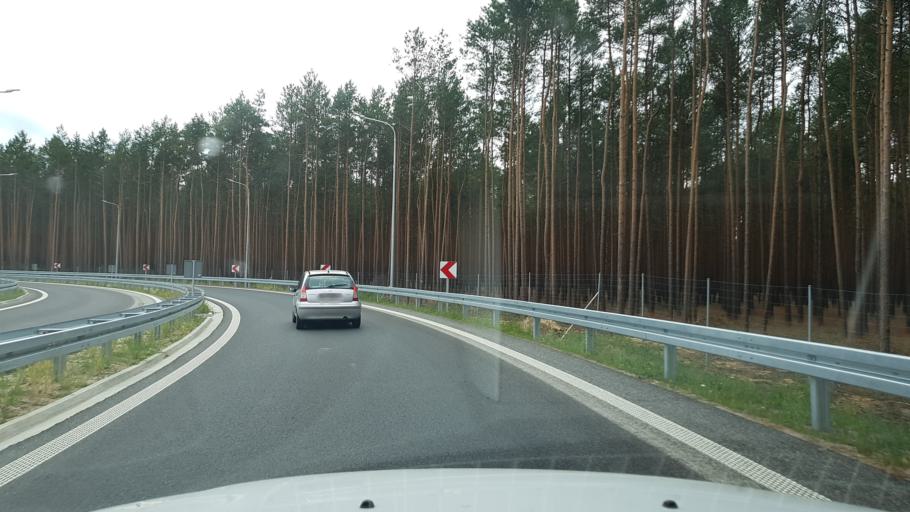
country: PL
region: West Pomeranian Voivodeship
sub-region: Powiat stargardzki
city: Kobylanka
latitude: 53.4268
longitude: 14.7675
